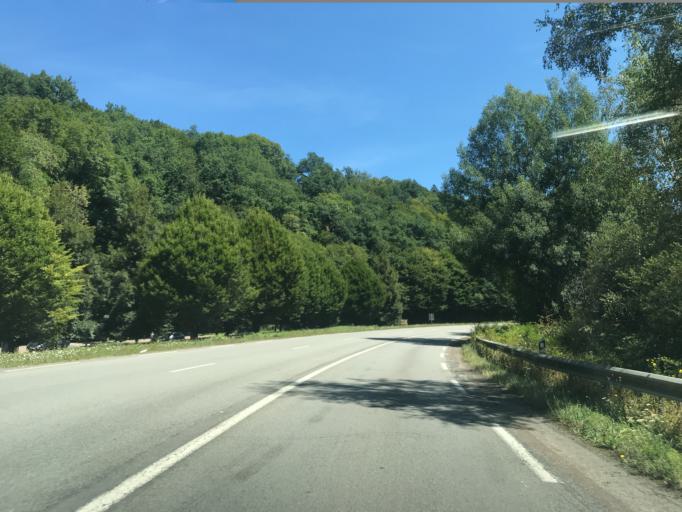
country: FR
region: Limousin
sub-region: Departement de la Correze
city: Chameyrat
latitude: 45.2322
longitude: 1.7162
